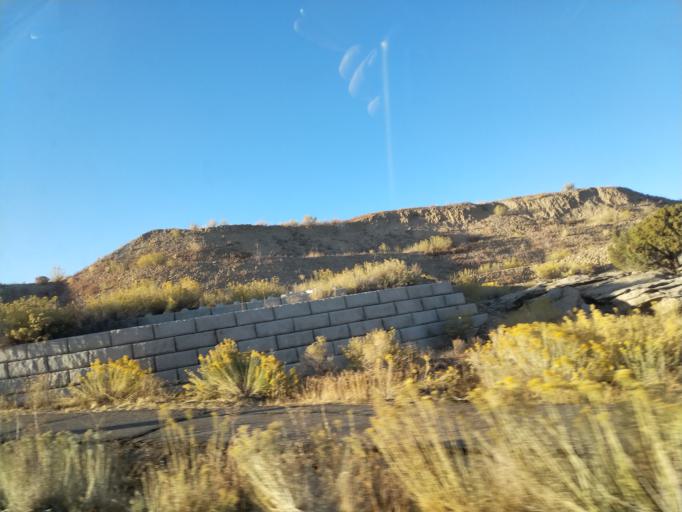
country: US
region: Colorado
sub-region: Mesa County
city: Redlands
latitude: 39.0568
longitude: -108.6158
